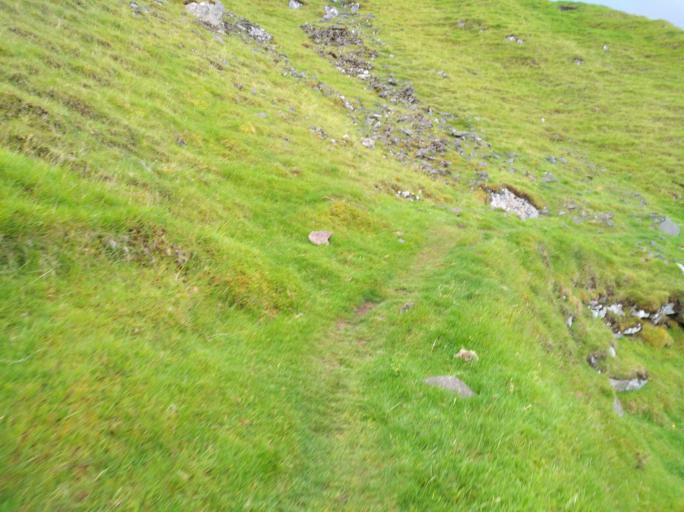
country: FO
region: Eysturoy
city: Fuglafjordur
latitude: 62.2882
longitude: -6.8800
